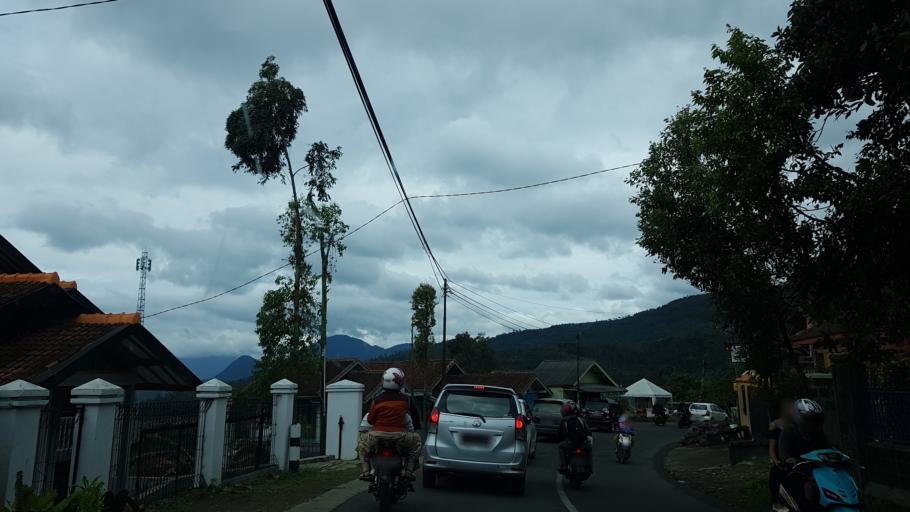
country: ID
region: West Java
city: Banjar
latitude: -7.1227
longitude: 107.4308
